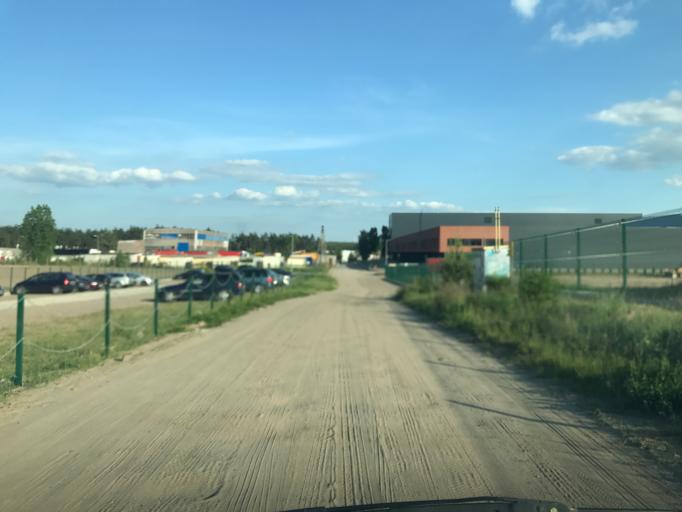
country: PL
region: Kujawsko-Pomorskie
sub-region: Powiat brodnicki
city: Brodnica
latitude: 53.2761
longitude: 19.4224
